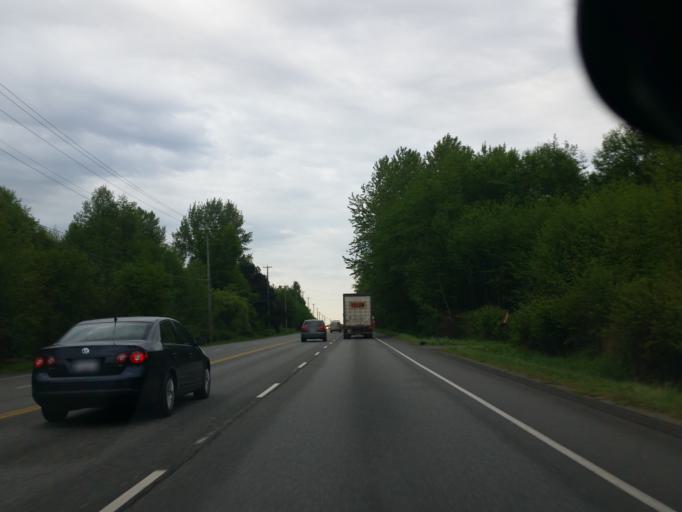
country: CA
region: British Columbia
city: Walnut Grove
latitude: 49.1394
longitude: -122.6684
